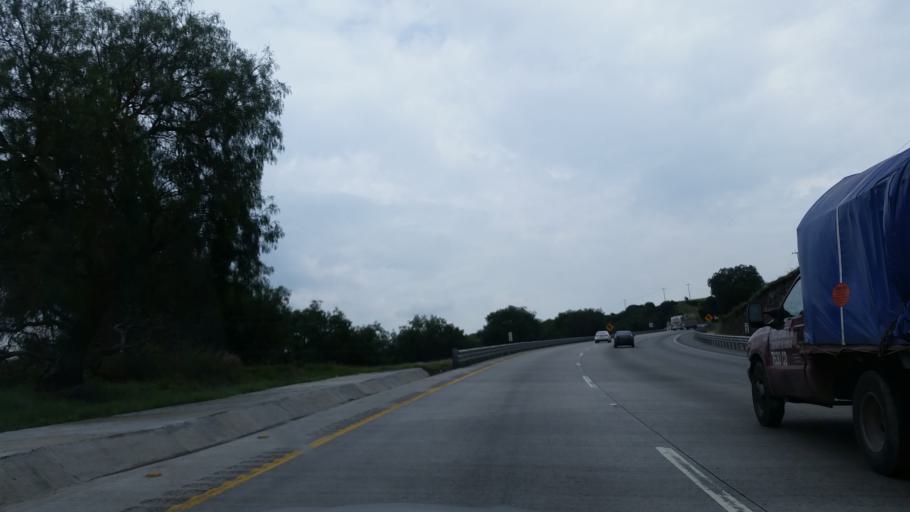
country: MX
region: Hidalgo
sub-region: Tepeji del Rio de Ocampo
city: Cantera de Villagran
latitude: 19.8609
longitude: -99.3162
